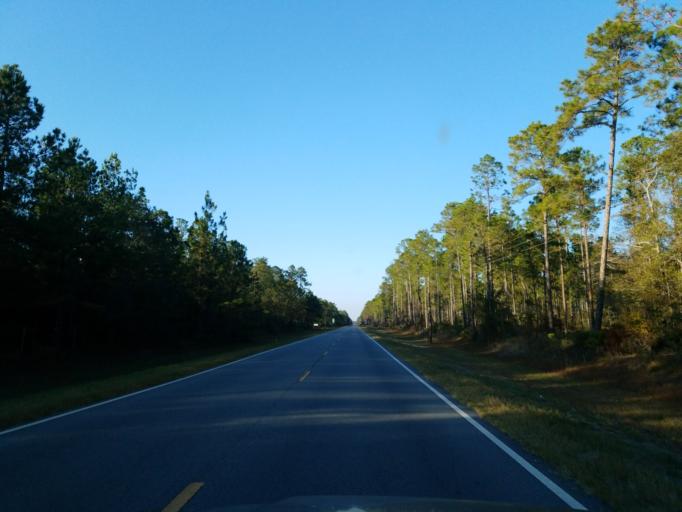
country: US
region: Georgia
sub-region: Lanier County
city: Lakeland
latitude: 31.1004
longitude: -83.0794
